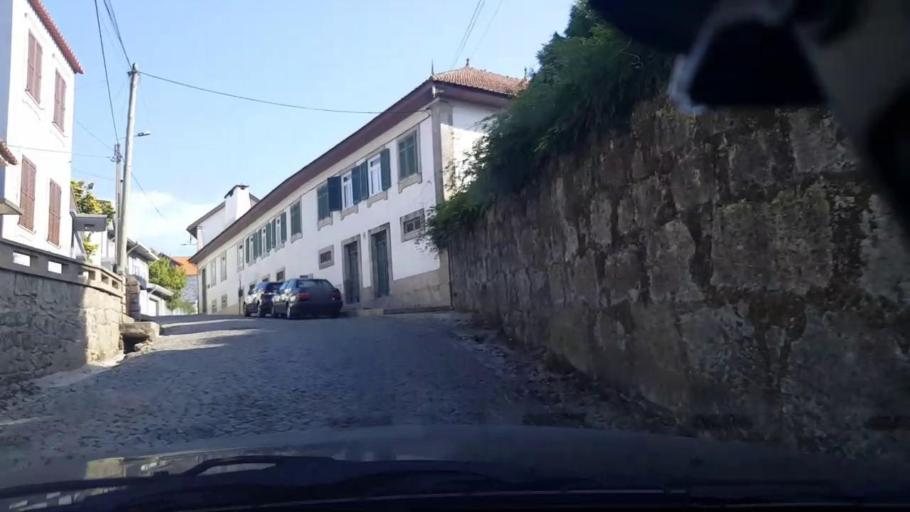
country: PT
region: Porto
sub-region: Maia
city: Gemunde
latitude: 41.2767
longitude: -8.6706
